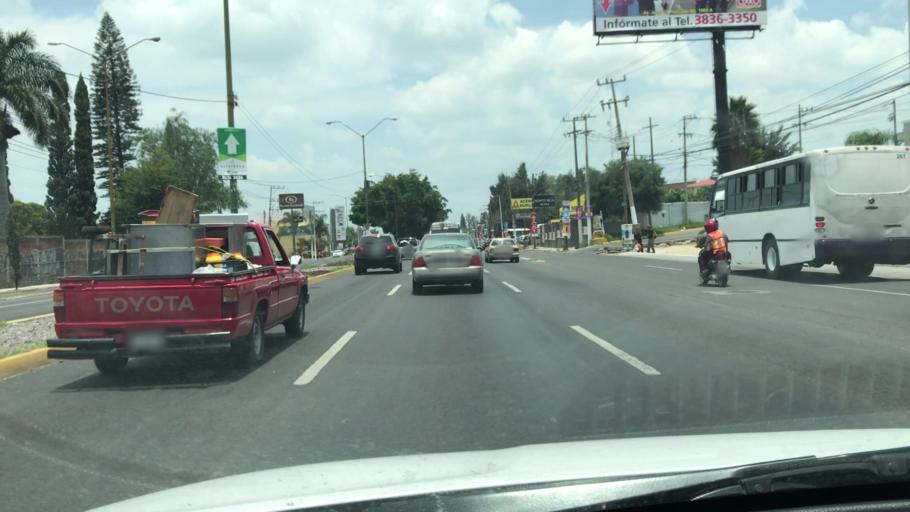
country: MX
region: Jalisco
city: Nuevo Mexico
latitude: 20.7491
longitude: -103.4182
